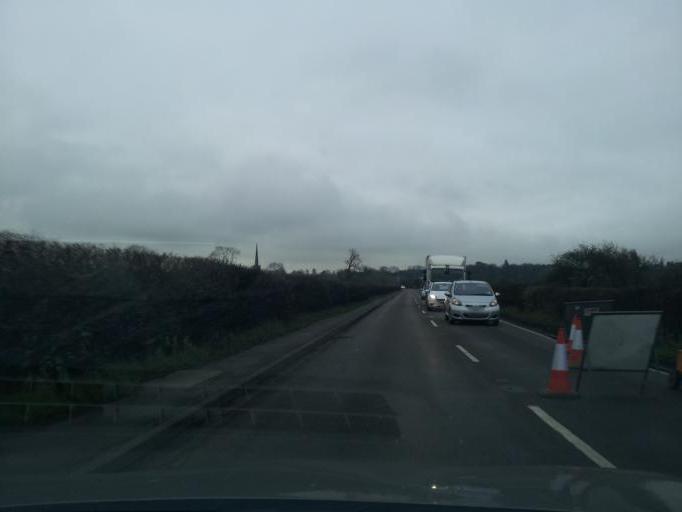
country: GB
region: England
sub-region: Derbyshire
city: Repton
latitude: 52.8470
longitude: -1.5605
